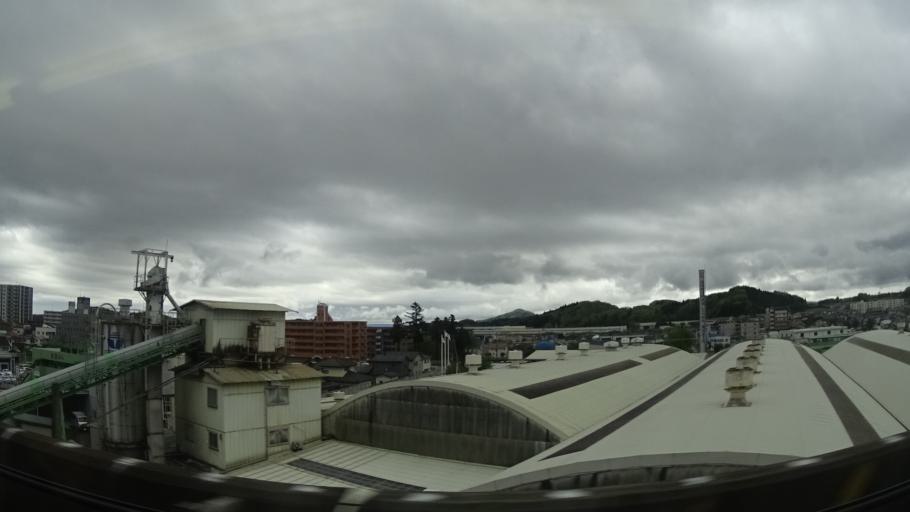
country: JP
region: Tochigi
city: Kuroiso
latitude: 37.1209
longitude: 140.1867
